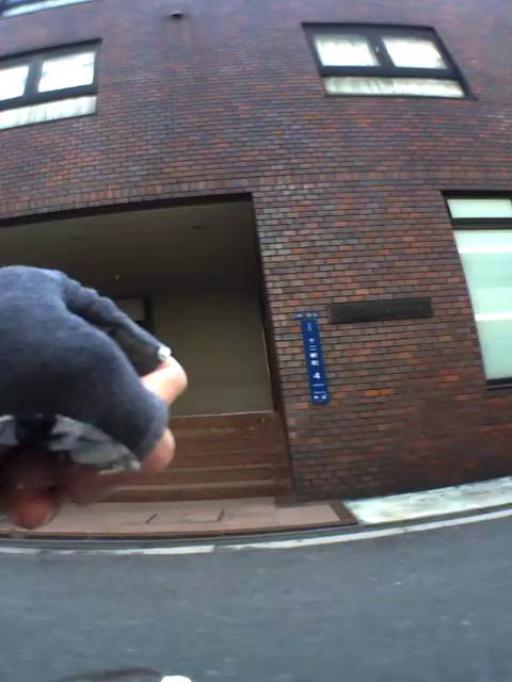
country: JP
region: Osaka
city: Osaka-shi
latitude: 34.6772
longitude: 135.5154
